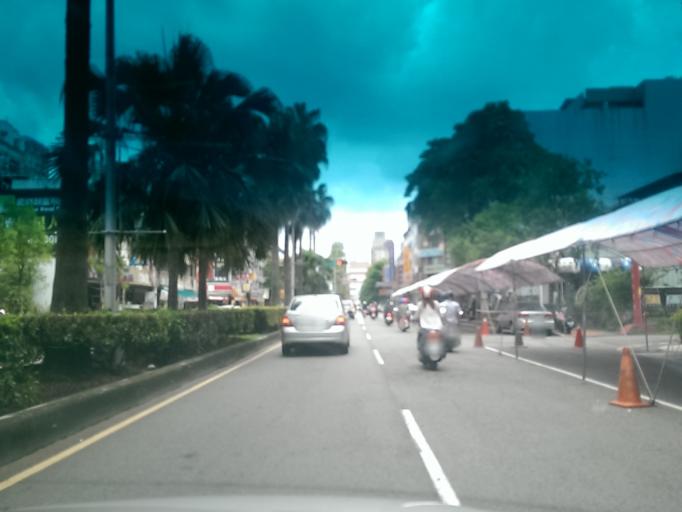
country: TW
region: Taiwan
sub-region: Taichung City
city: Taichung
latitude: 24.1629
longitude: 120.6694
